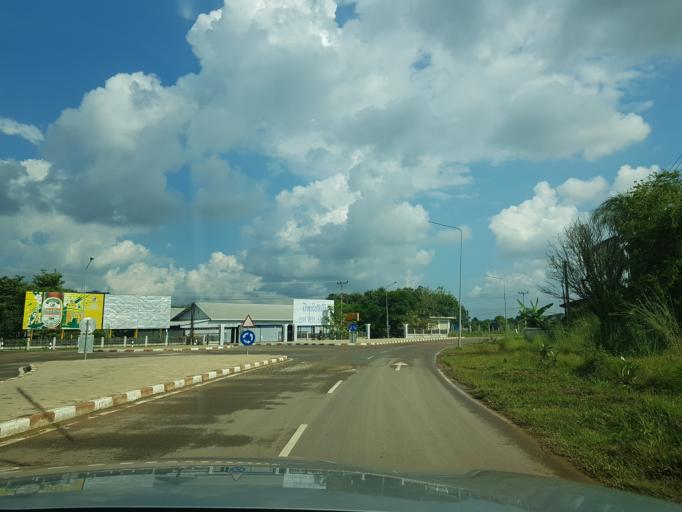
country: TH
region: Nong Khai
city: Sangkhom
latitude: 18.0911
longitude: 102.2898
